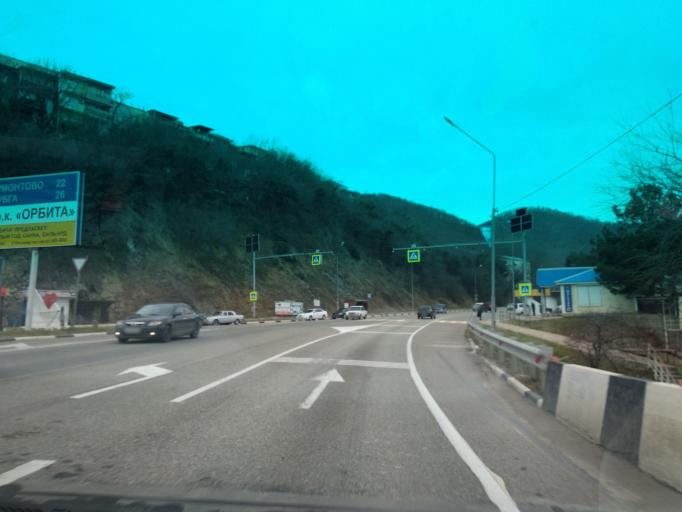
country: RU
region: Krasnodarskiy
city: Ol'ginka
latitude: 44.1994
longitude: 38.8883
